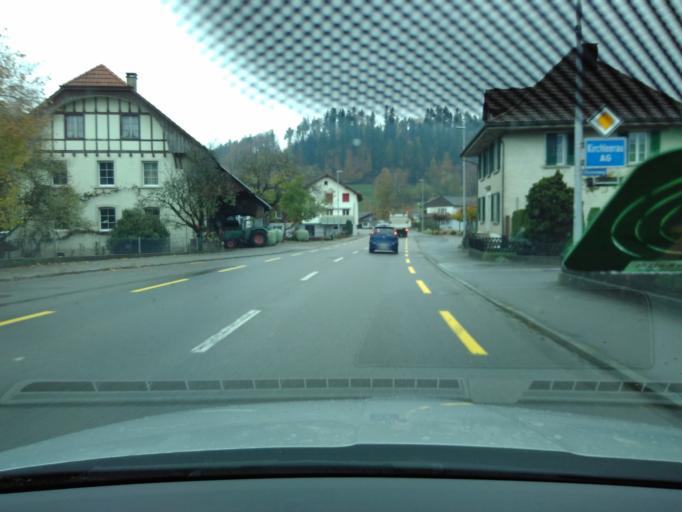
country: CH
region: Aargau
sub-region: Bezirk Zofingen
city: Kirchleerau
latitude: 47.2717
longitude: 8.0647
